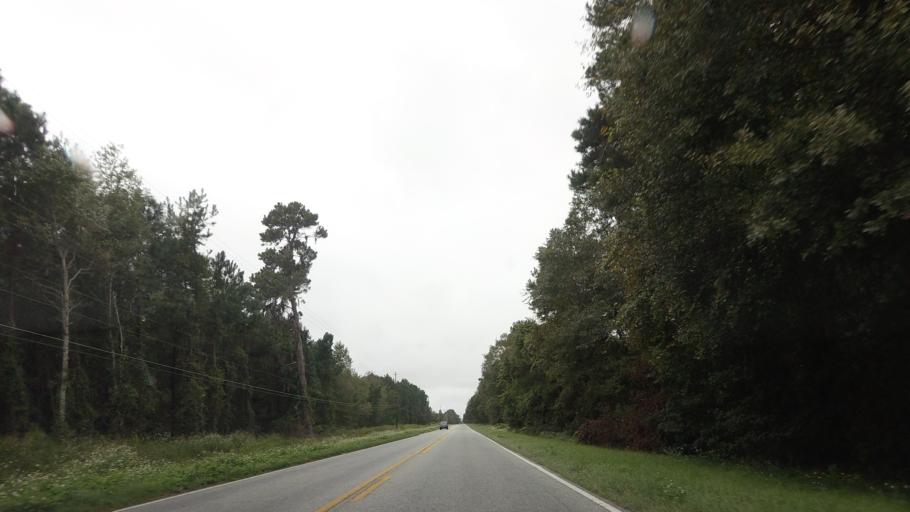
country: US
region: Georgia
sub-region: Lowndes County
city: Valdosta
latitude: 30.8146
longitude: -83.2464
